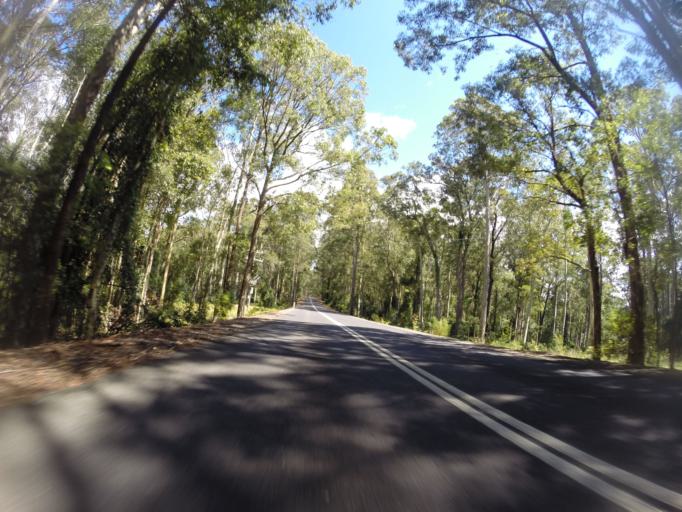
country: AU
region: New South Wales
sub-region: Eurobodalla
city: Batemans Bay
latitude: -35.6563
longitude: 150.2522
